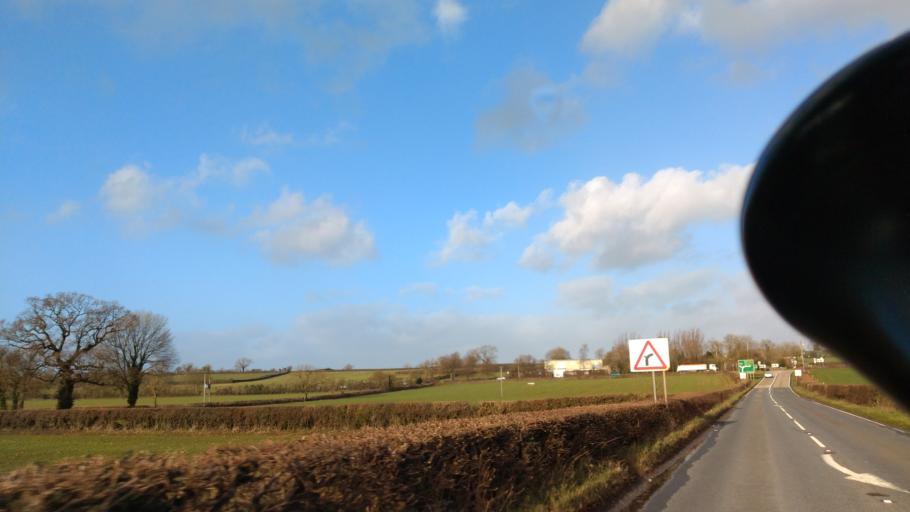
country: GB
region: England
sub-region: Somerset
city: Shepton Mallet
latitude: 51.1670
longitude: -2.5383
